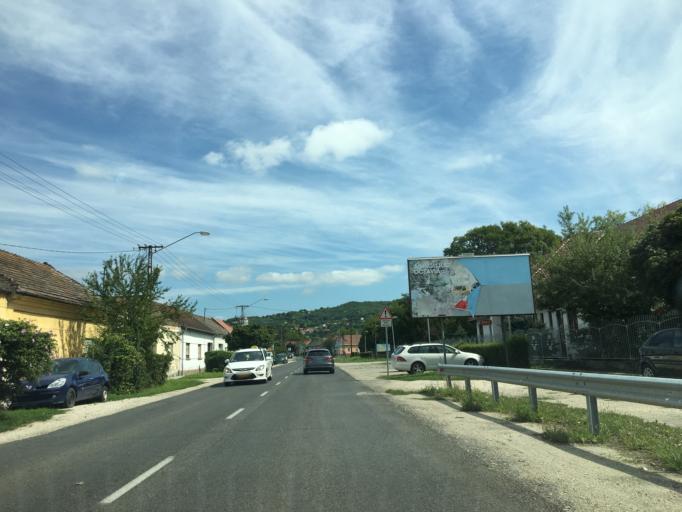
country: HU
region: Komarom-Esztergom
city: Esztergom
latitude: 47.7811
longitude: 18.7350
